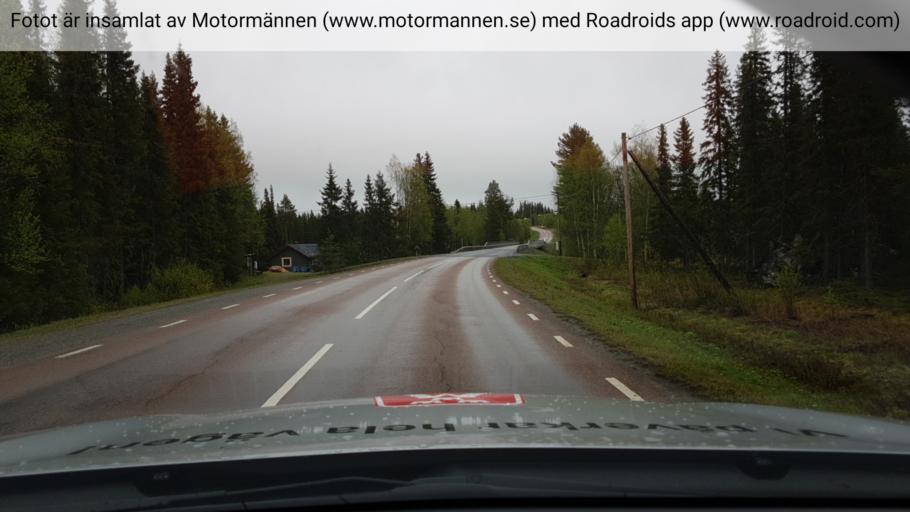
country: SE
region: Jaemtland
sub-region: Krokoms Kommun
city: Valla
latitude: 63.1615
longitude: 13.9802
